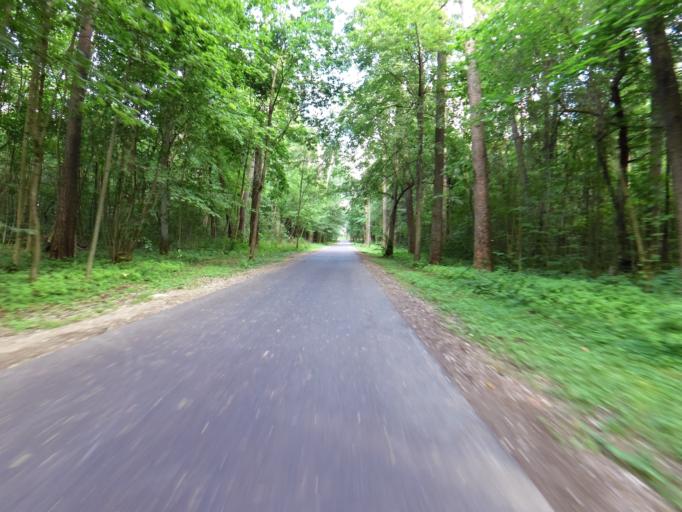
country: LT
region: Vilnius County
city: Vilkpede
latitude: 54.6881
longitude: 25.2403
